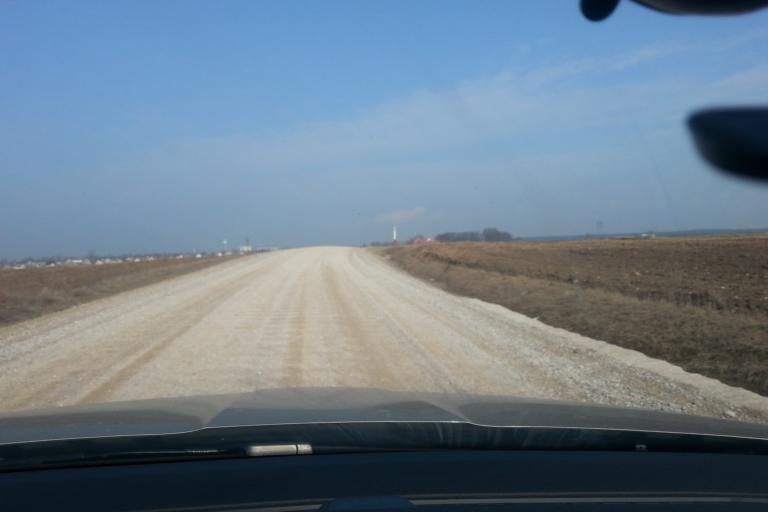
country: LT
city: Trakai
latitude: 54.5976
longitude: 24.9784
